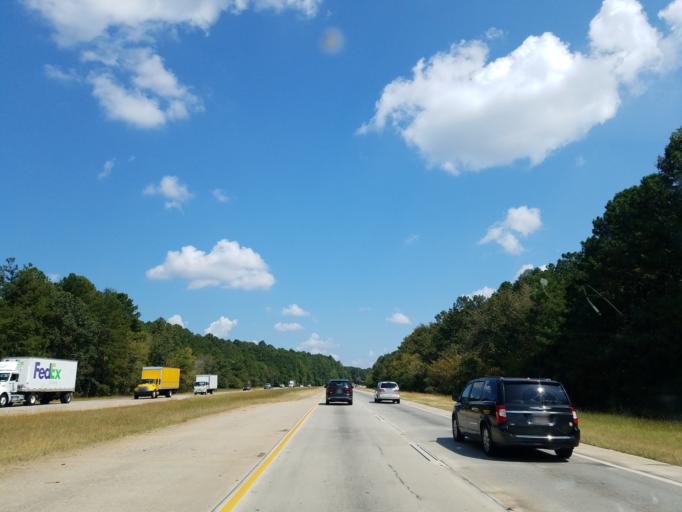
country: US
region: Georgia
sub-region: Gwinnett County
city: Dacula
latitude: 33.9856
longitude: -83.9450
